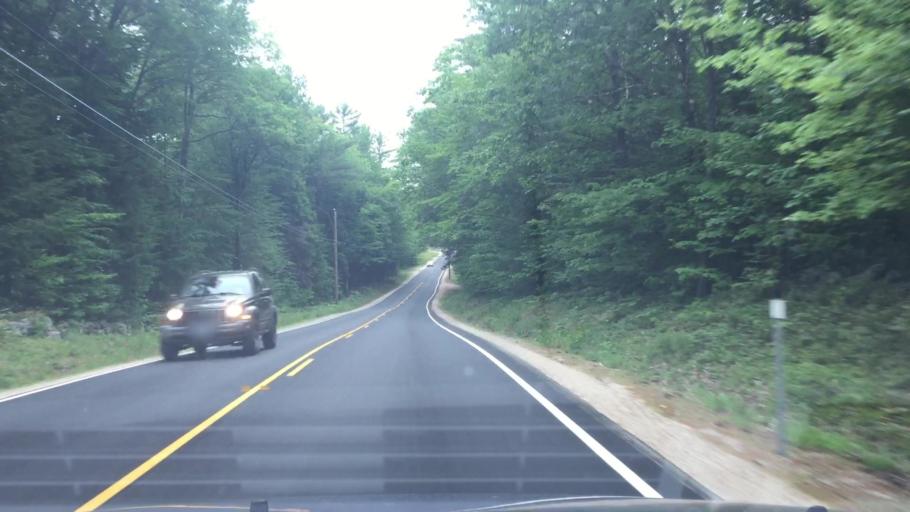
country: US
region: New Hampshire
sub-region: Carroll County
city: Freedom
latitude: 43.8333
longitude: -71.0775
